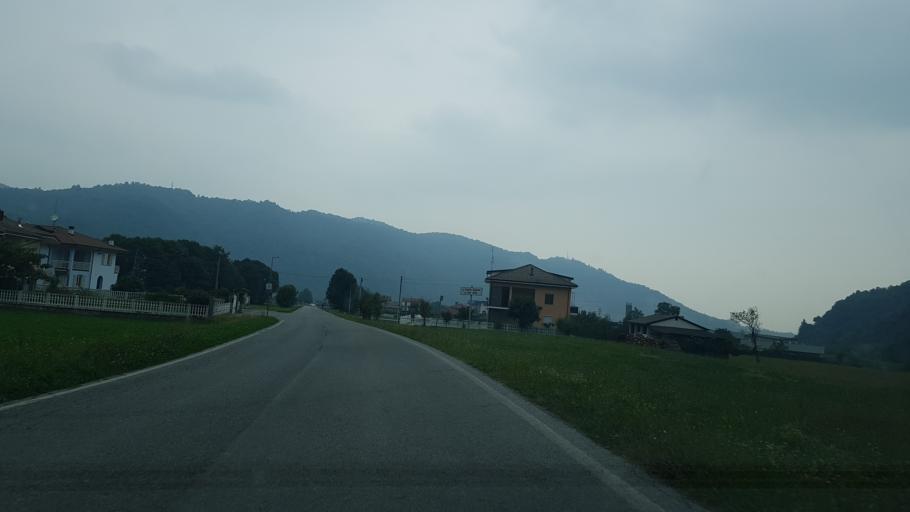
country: IT
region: Piedmont
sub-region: Provincia di Cuneo
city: Roccaforte Mondovi
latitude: 44.3087
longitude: 7.7456
